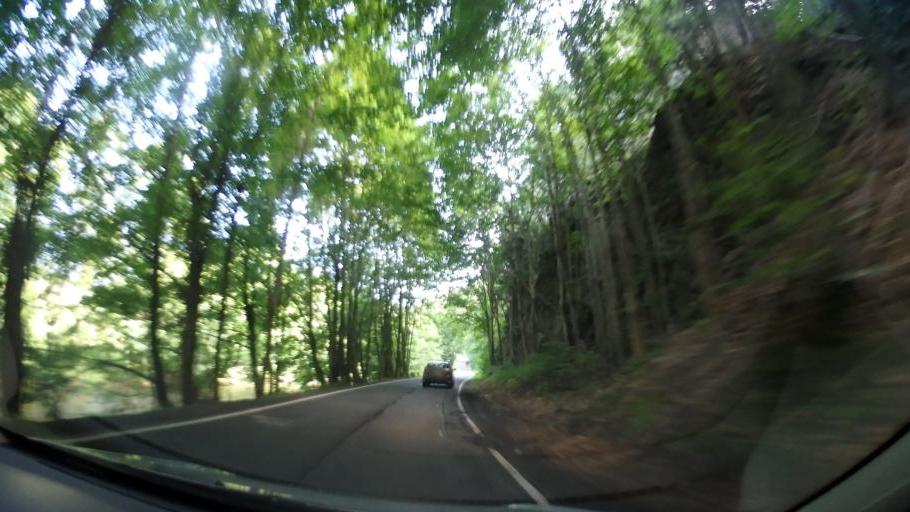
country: CZ
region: Olomoucky
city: Zabreh
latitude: 49.8628
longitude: 16.8205
